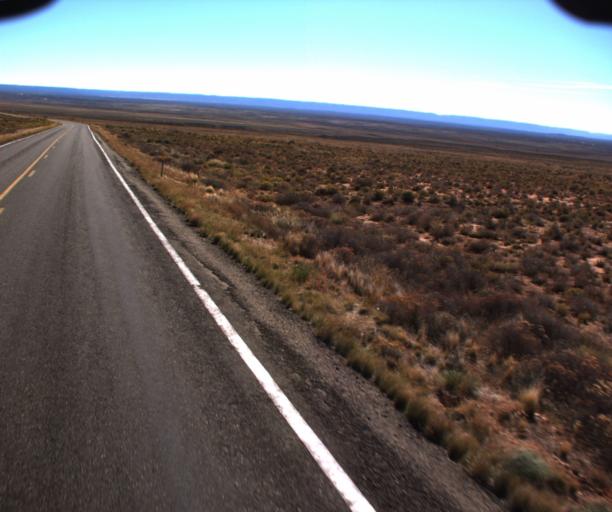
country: US
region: Arizona
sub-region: Coconino County
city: Fredonia
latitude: 36.9297
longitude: -112.4903
